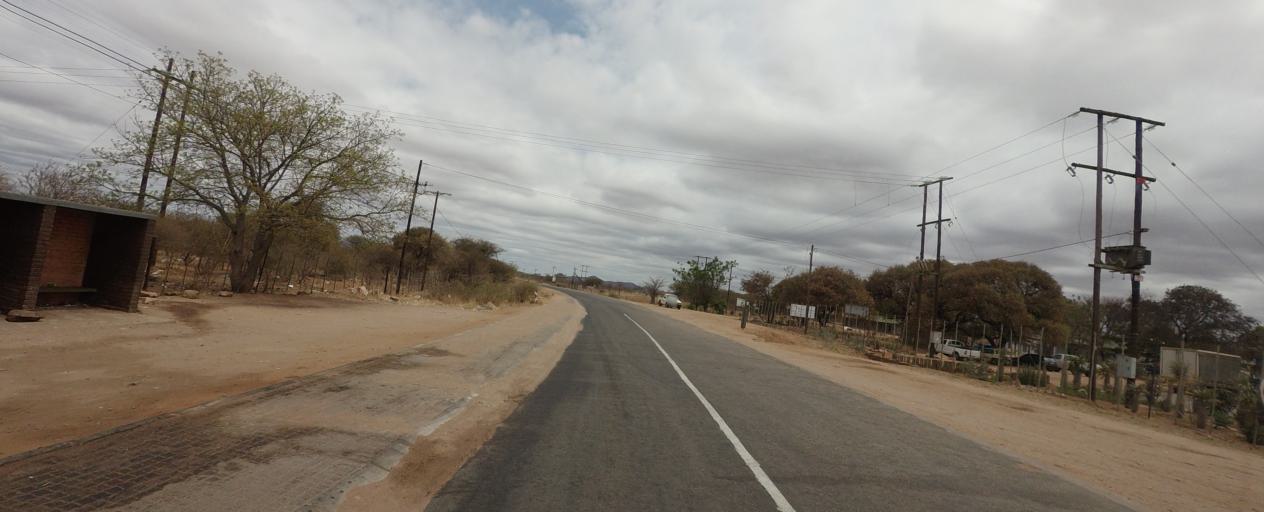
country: BW
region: Central
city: Mathathane
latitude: -22.6779
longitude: 29.1029
